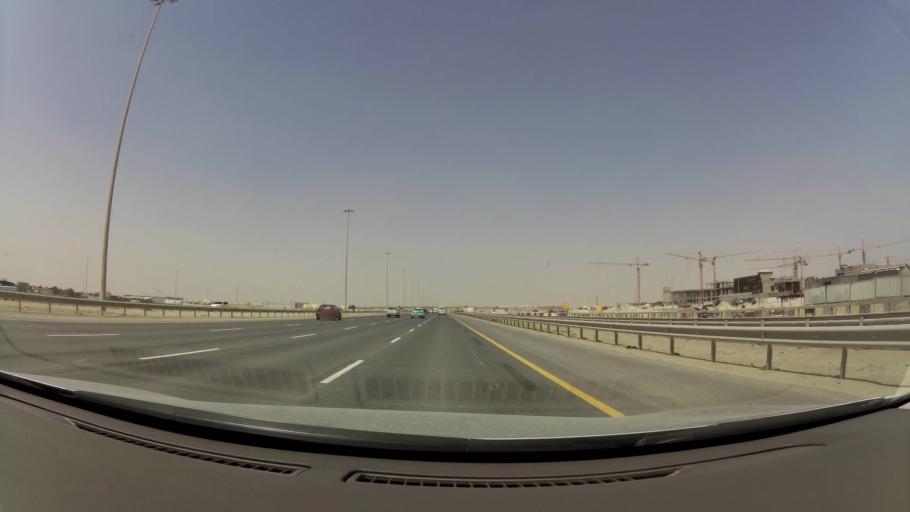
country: QA
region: Baladiyat Umm Salal
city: Umm Salal Muhammad
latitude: 25.4034
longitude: 51.4287
